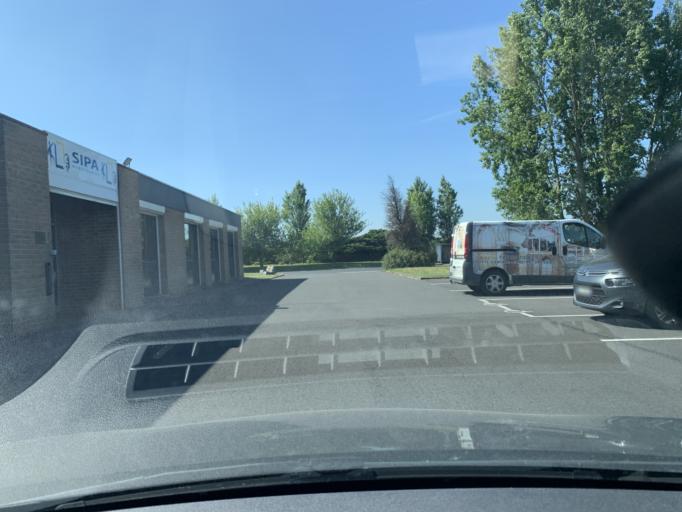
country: FR
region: Nord-Pas-de-Calais
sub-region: Departement du Nord
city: Rumilly-en-Cambresis
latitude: 50.1455
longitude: 3.2241
